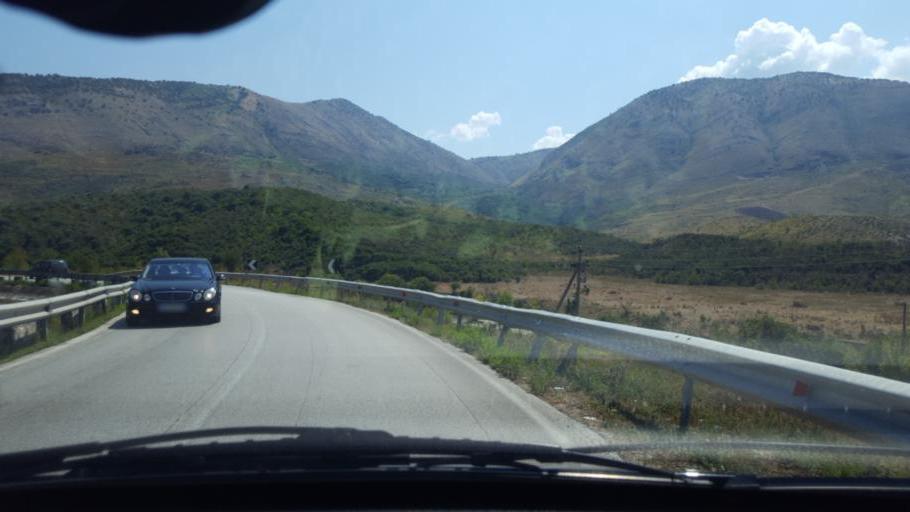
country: AL
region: Vlore
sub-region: Rrethi i Delvines
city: Mesopotam
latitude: 39.9085
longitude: 20.1240
